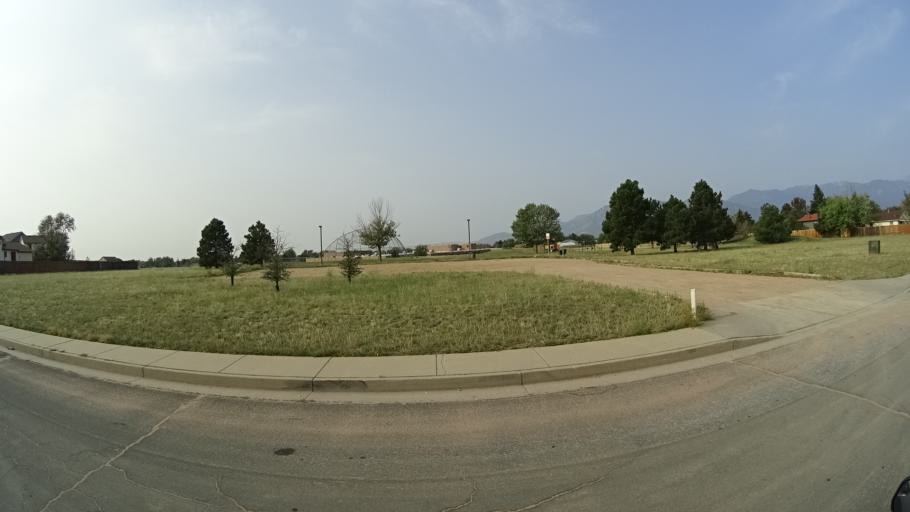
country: US
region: Colorado
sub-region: El Paso County
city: Stratmoor
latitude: 38.8062
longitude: -104.7401
